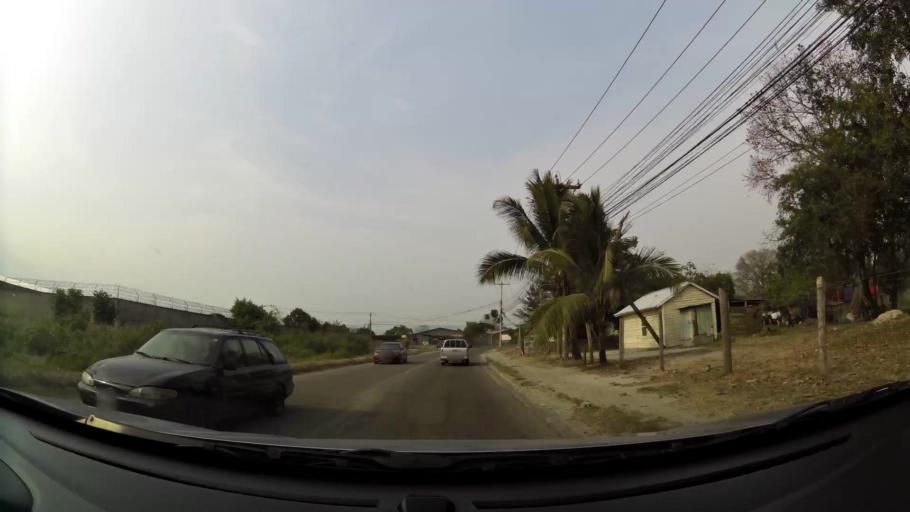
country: HN
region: Cortes
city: San Pedro Sula
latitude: 15.5383
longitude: -88.0124
